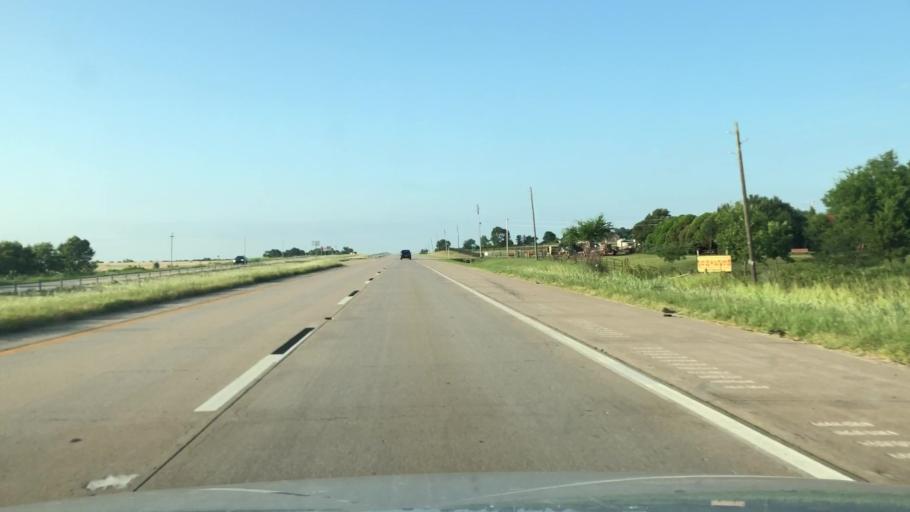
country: US
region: Oklahoma
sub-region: Osage County
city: Skiatook
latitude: 36.4687
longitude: -95.9207
